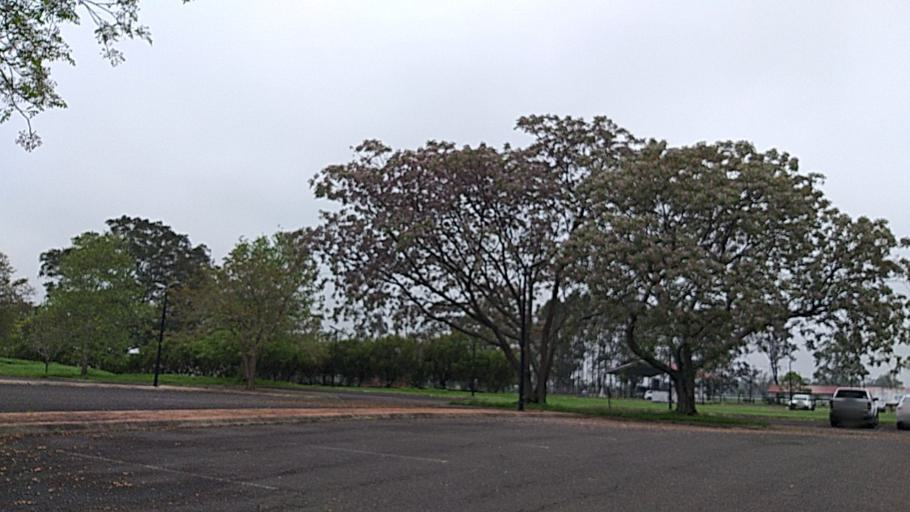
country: AU
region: New South Wales
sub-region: Hawkesbury
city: Richmond
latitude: -33.6120
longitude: 150.7553
